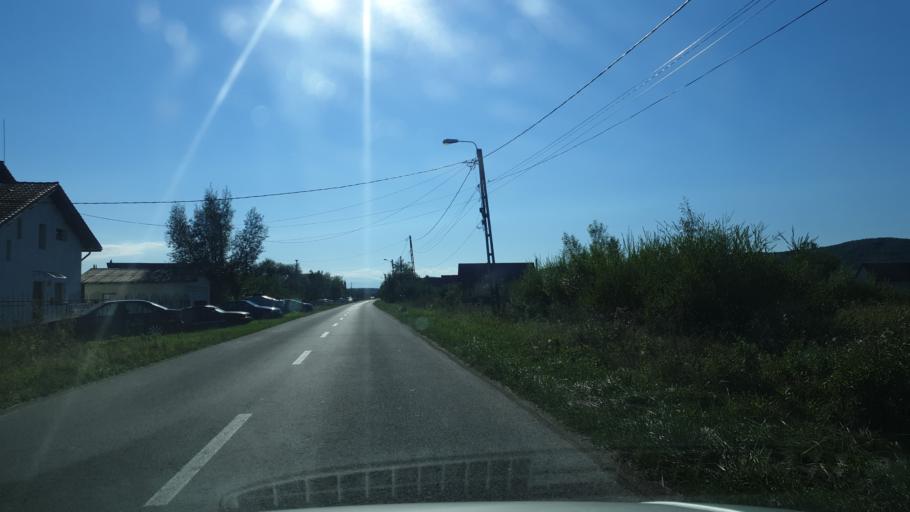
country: RO
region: Covasna
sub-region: Comuna Ilieni
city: Ilieni
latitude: 45.7664
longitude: 25.7331
